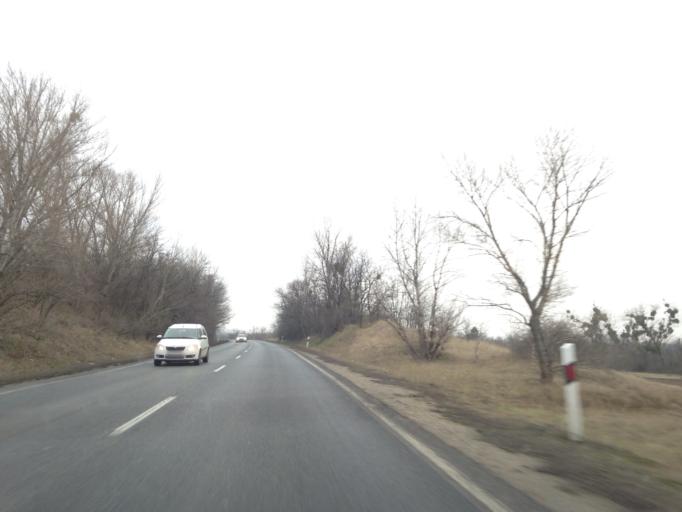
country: HU
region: Komarom-Esztergom
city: Szomod
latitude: 47.6854
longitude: 18.3127
